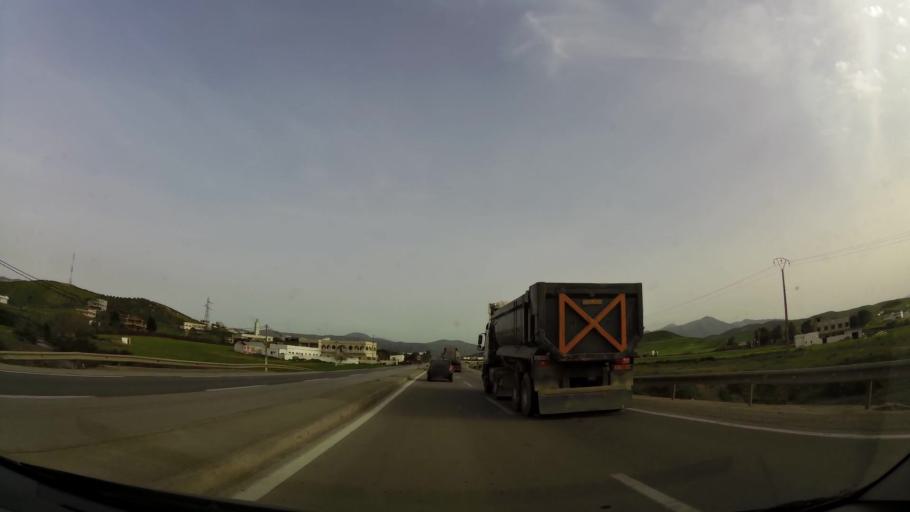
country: MA
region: Tanger-Tetouan
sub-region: Tanger-Assilah
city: Dar Chaoui
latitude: 35.5866
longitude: -5.6416
